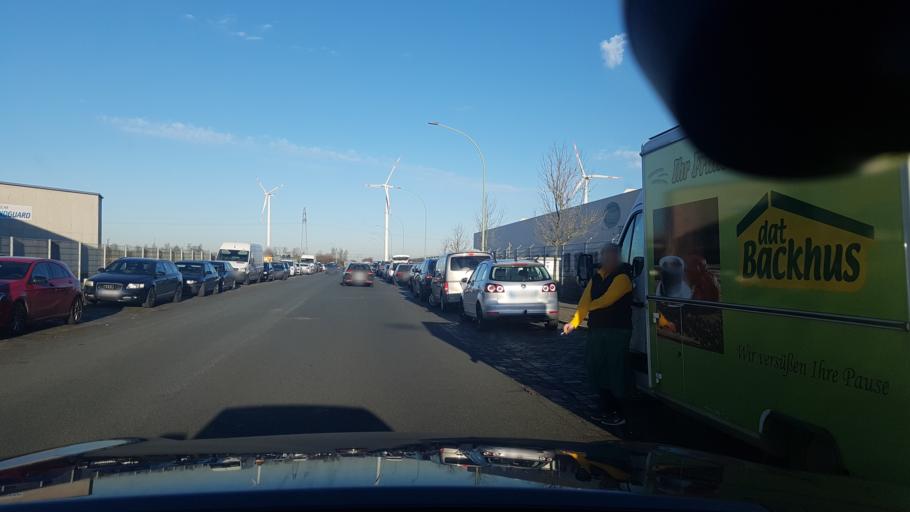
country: DE
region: Lower Saxony
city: Langen
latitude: 53.5949
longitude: 8.5496
